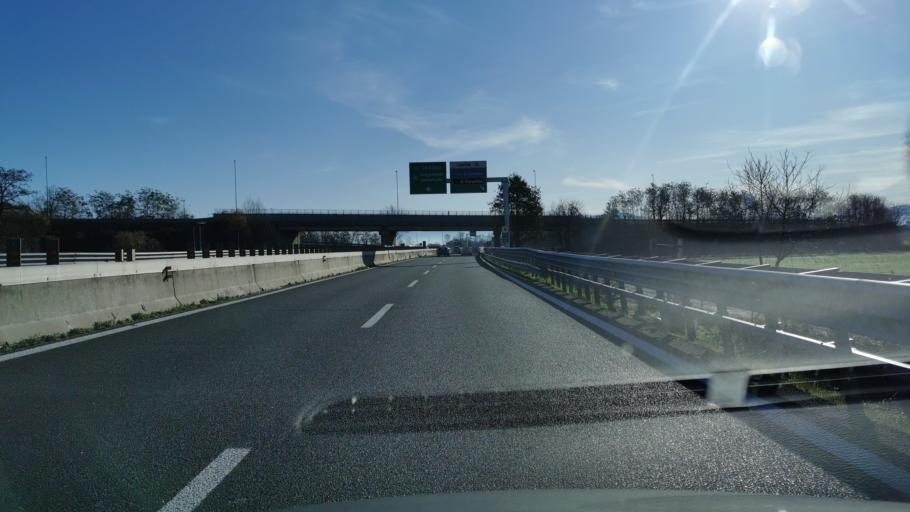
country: IT
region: Piedmont
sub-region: Provincia di Torino
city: Borgaro Torinese
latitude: 45.1709
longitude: 7.6777
